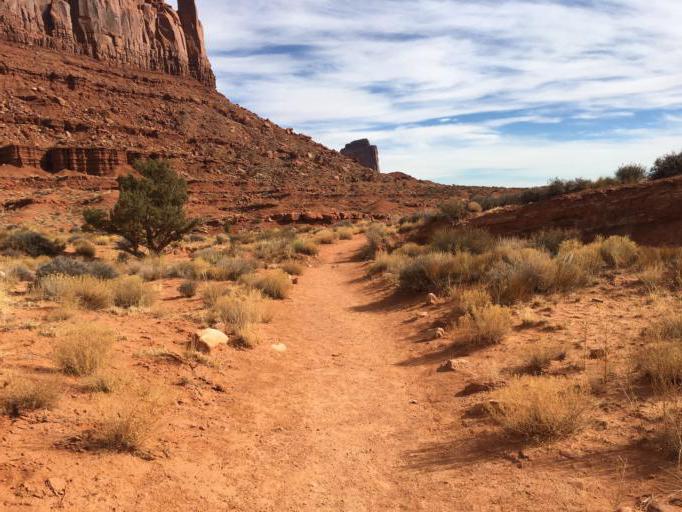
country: US
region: Arizona
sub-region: Navajo County
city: Kayenta
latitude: 36.9881
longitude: -110.1011
